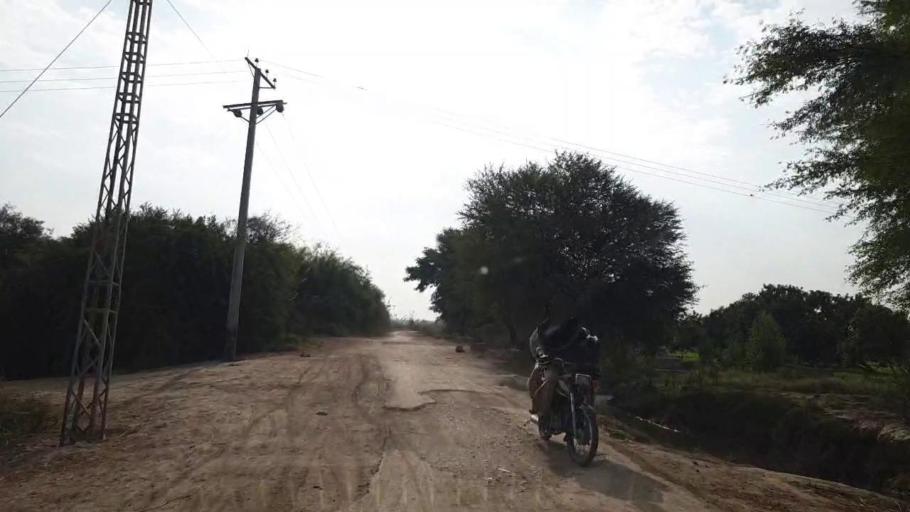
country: PK
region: Sindh
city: Tando Muhammad Khan
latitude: 25.0345
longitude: 68.4376
